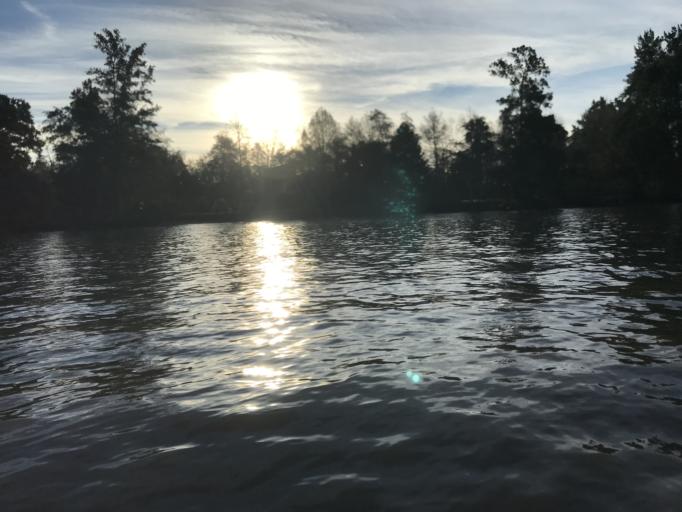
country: AR
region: Buenos Aires
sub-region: Partido de Tigre
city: Tigre
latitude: -34.3823
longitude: -58.5757
